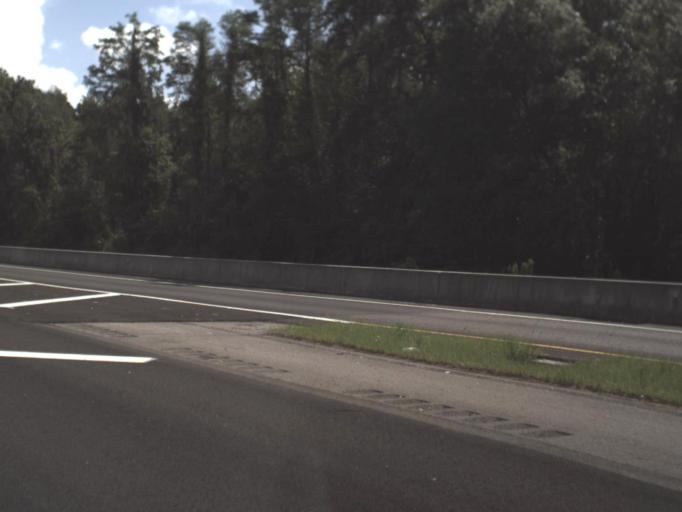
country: US
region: Florida
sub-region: Pasco County
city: Wesley Chapel
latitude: 28.2400
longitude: -82.3519
